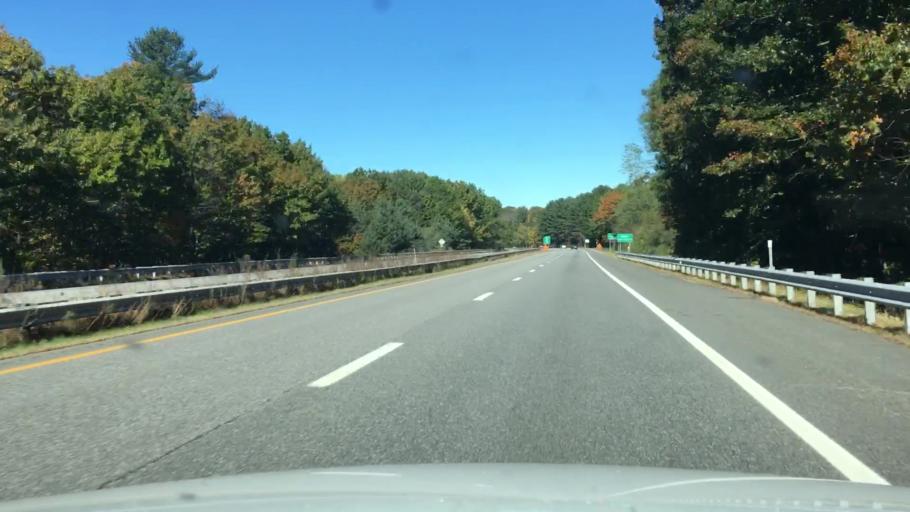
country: US
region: New Hampshire
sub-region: Strafford County
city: Dover
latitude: 43.1696
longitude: -70.8602
